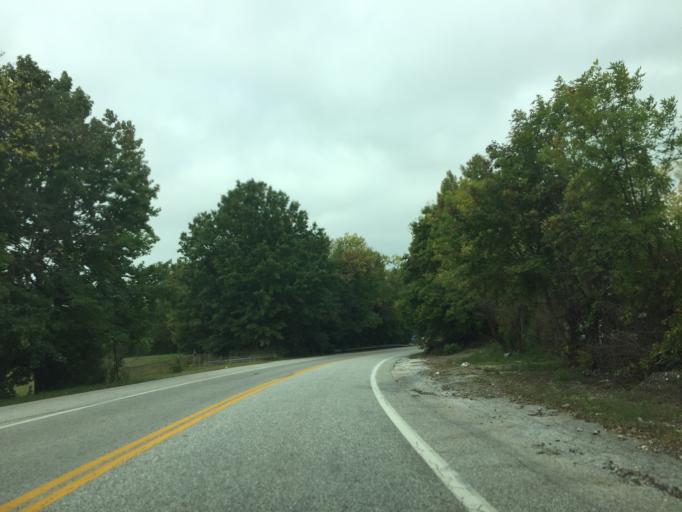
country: US
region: Maryland
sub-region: Baltimore County
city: Rossville
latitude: 39.3272
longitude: -76.4720
